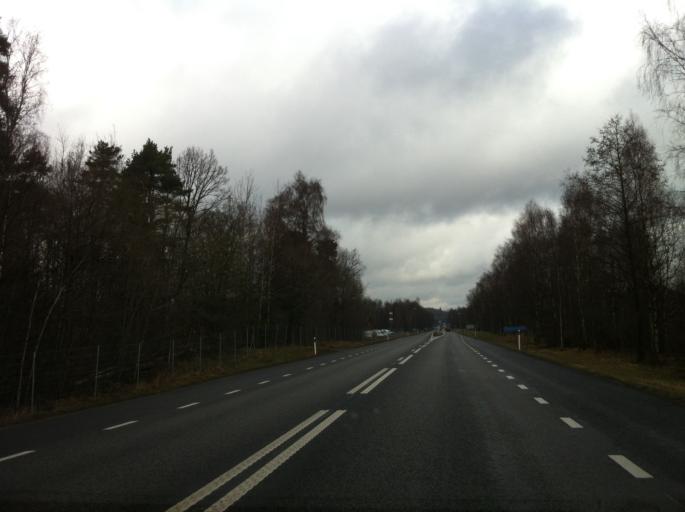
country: SE
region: Halland
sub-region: Halmstads Kommun
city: Oskarstrom
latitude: 56.7880
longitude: 12.9586
